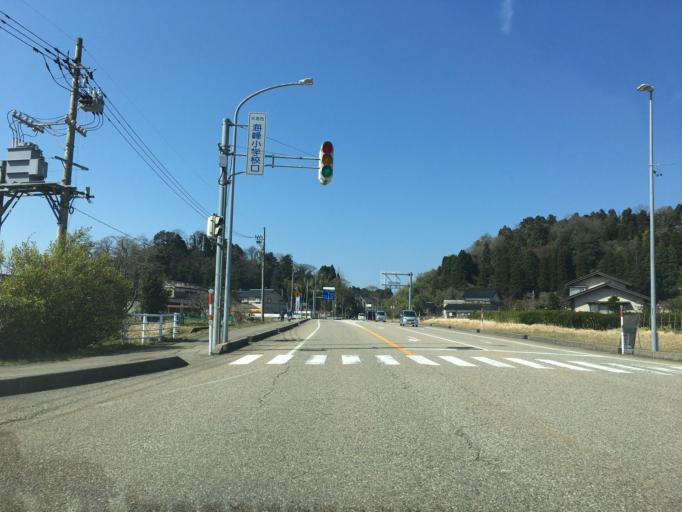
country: JP
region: Toyama
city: Himi
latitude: 36.8837
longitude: 136.9904
